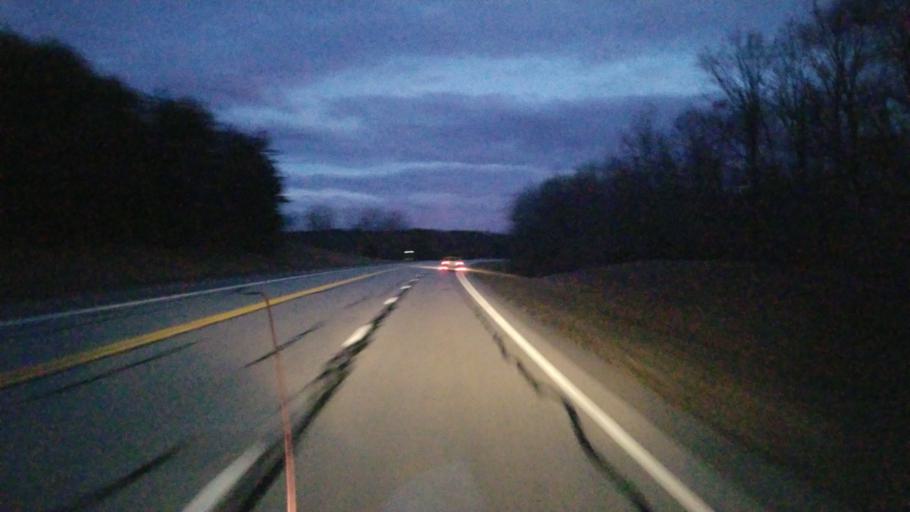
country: US
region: Tennessee
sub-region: Sequatchie County
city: Dunlap
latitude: 35.5037
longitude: -85.4744
